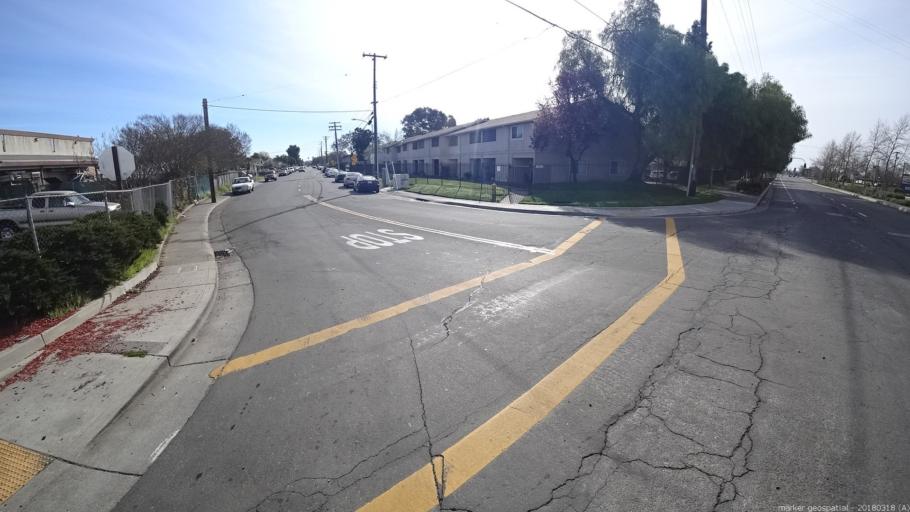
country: US
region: California
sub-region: Sacramento County
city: Parkway
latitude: 38.5045
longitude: -121.4637
